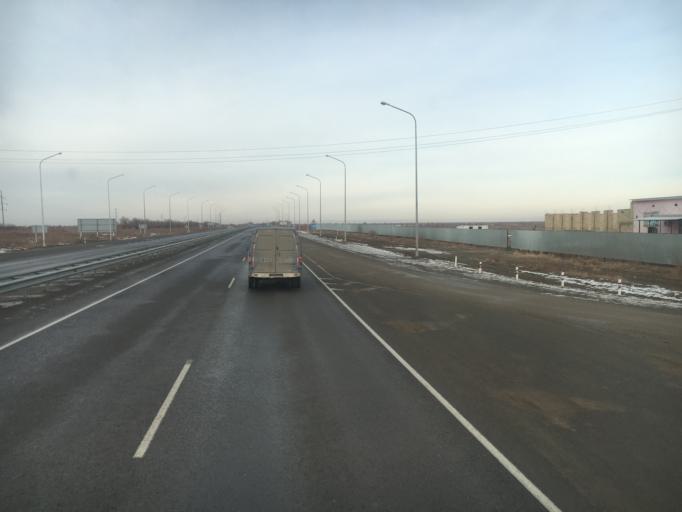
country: KZ
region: Qyzylorda
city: Shieli
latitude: 44.1401
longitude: 66.9645
